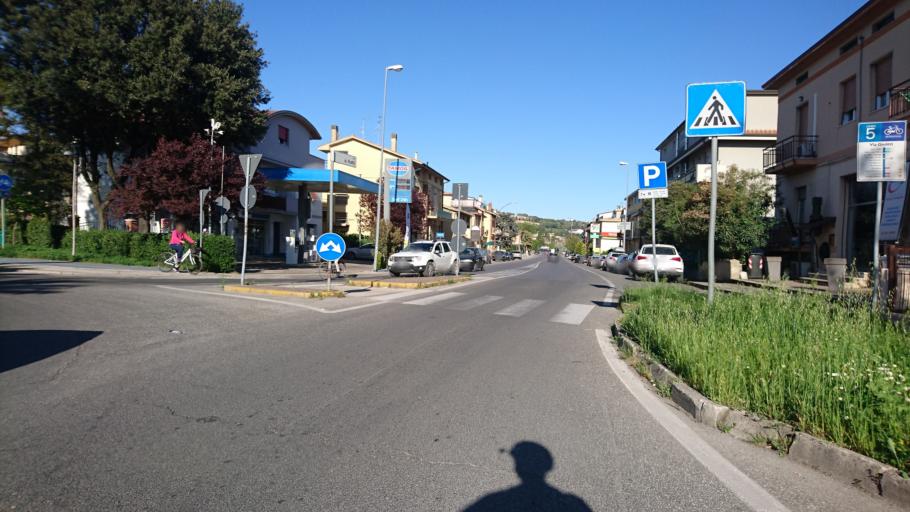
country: IT
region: The Marches
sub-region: Provincia di Pesaro e Urbino
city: Pesaro
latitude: 43.8958
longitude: 12.9104
